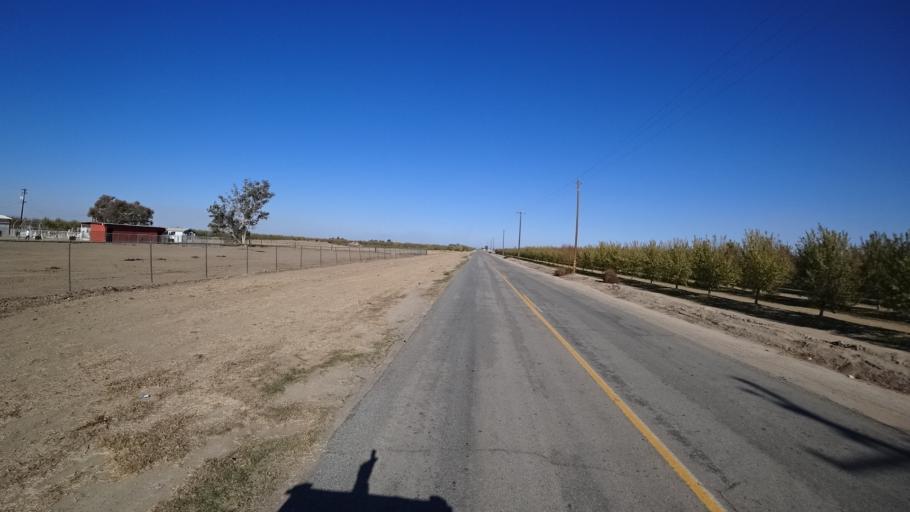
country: US
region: California
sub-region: Kern County
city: Greenfield
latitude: 35.2528
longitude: -119.0568
